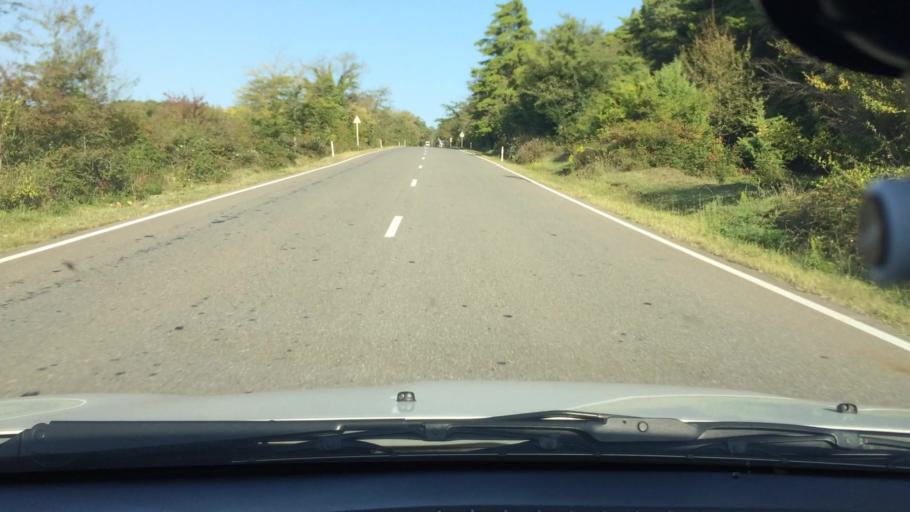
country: GE
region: Imereti
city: Kutaisi
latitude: 42.2429
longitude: 42.7623
